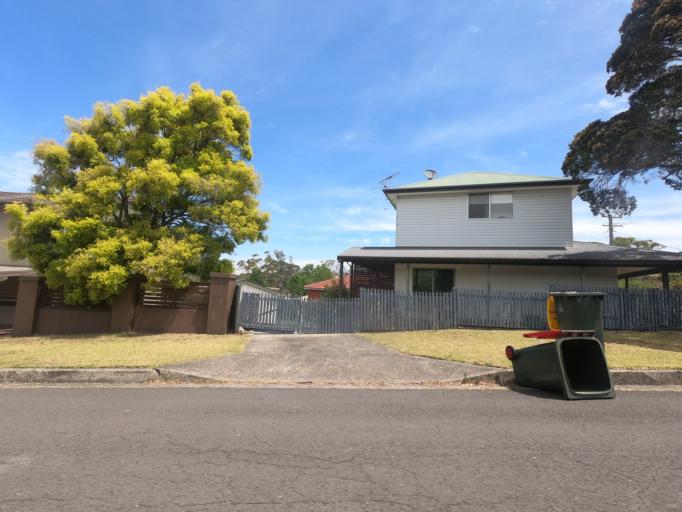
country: AU
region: New South Wales
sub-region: Wollongong
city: Mount Ousley
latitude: -34.3926
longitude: 150.8831
